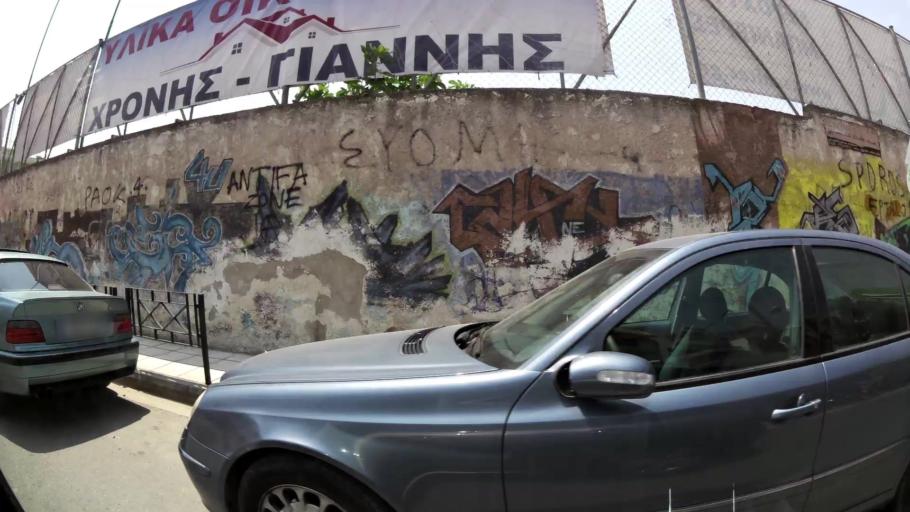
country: GR
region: Central Macedonia
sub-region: Nomos Thessalonikis
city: Evosmos
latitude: 40.6671
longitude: 22.9085
